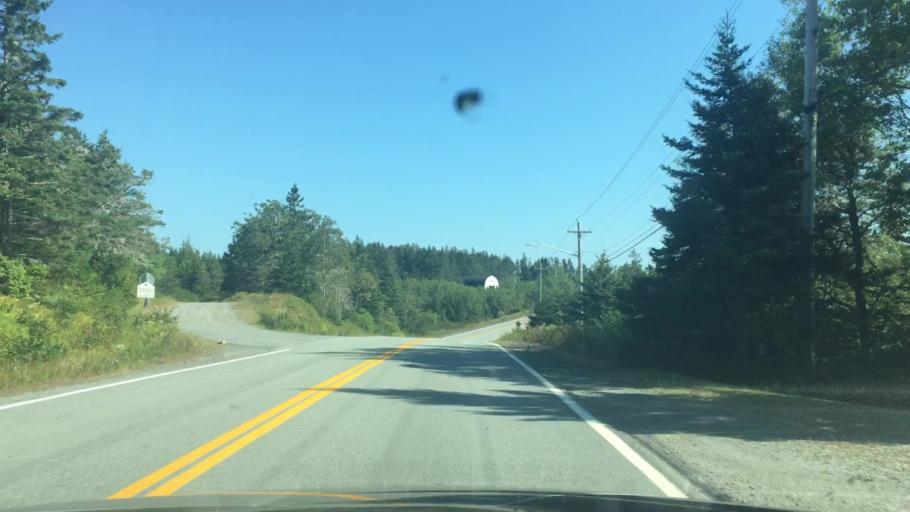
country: CA
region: Nova Scotia
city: New Glasgow
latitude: 44.8249
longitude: -62.6298
